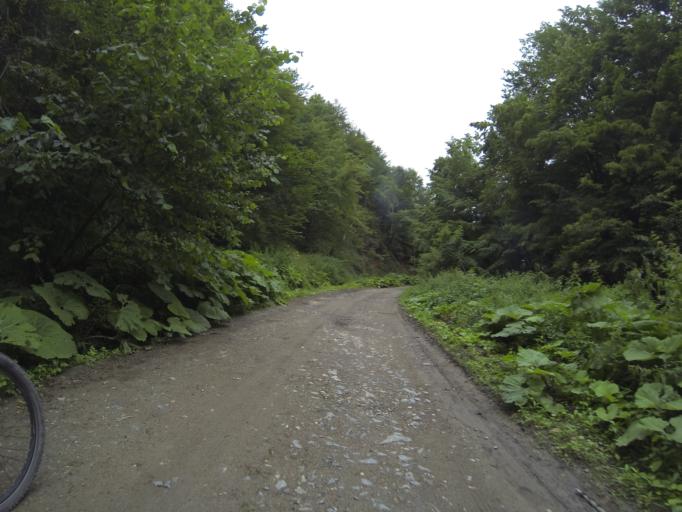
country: RO
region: Brasov
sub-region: Comuna Sinca Veche
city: Sinca Veche
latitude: 45.6869
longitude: 25.1478
